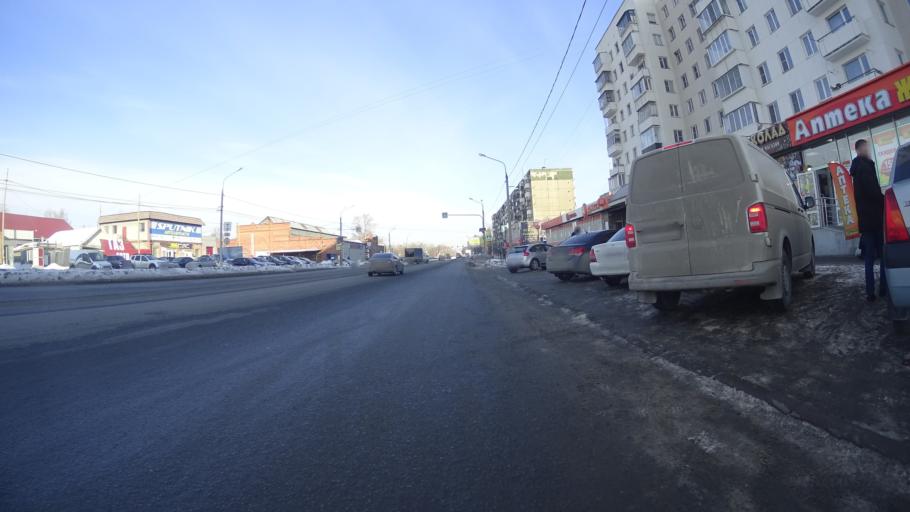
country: RU
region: Chelyabinsk
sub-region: Gorod Chelyabinsk
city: Chelyabinsk
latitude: 55.1866
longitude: 61.4361
